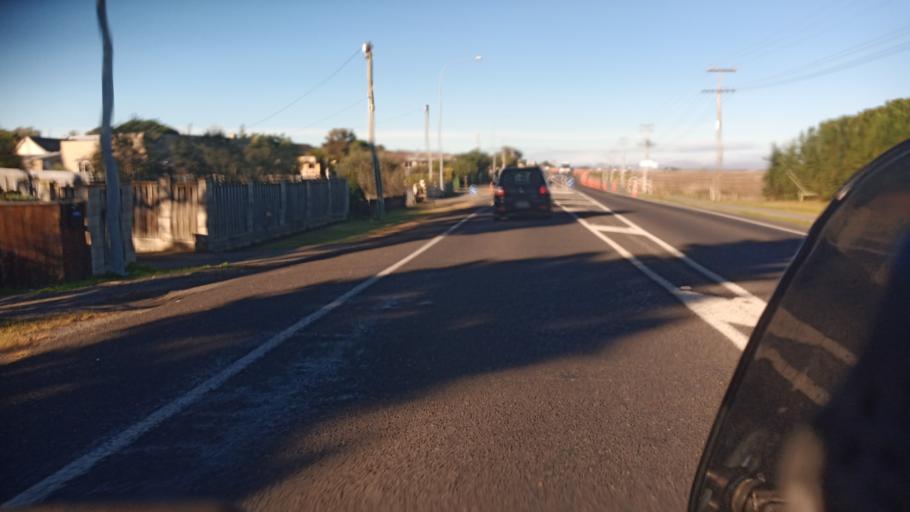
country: NZ
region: Hawke's Bay
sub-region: Napier City
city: Napier
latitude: -39.4390
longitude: 176.8704
